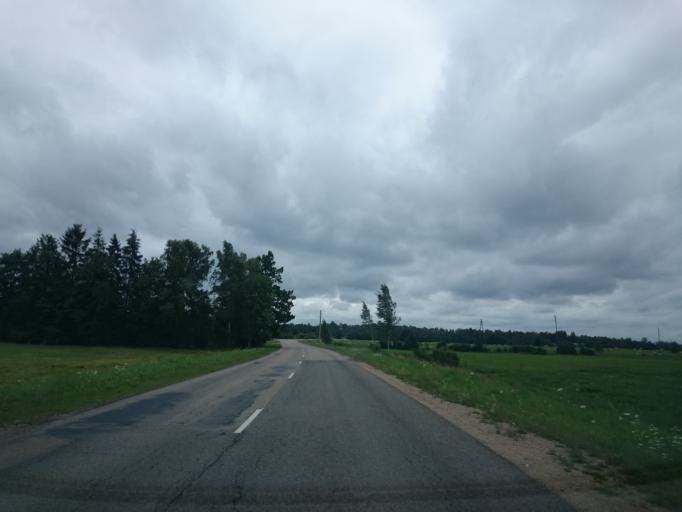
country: LV
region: Pavilostas
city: Pavilosta
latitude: 56.8709
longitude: 21.2247
